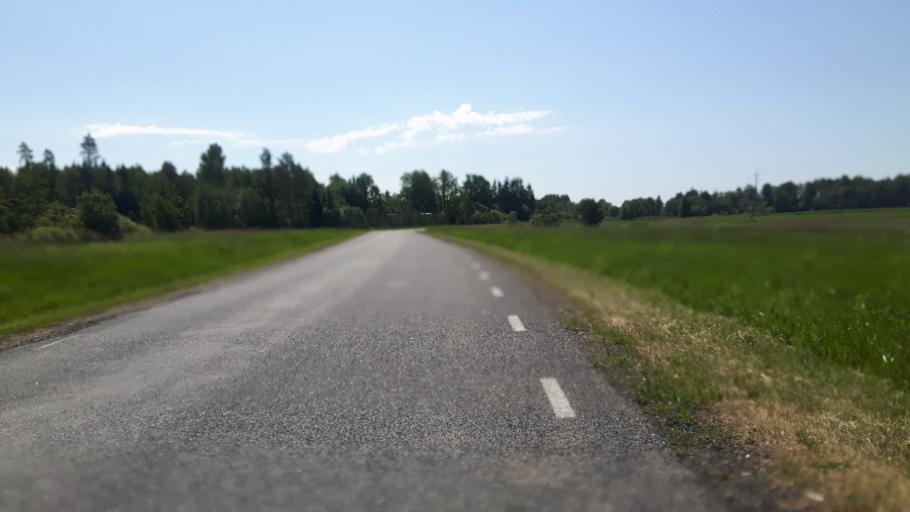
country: EE
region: Paernumaa
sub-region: Vaendra vald (alev)
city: Vandra
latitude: 58.6054
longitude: 25.0216
